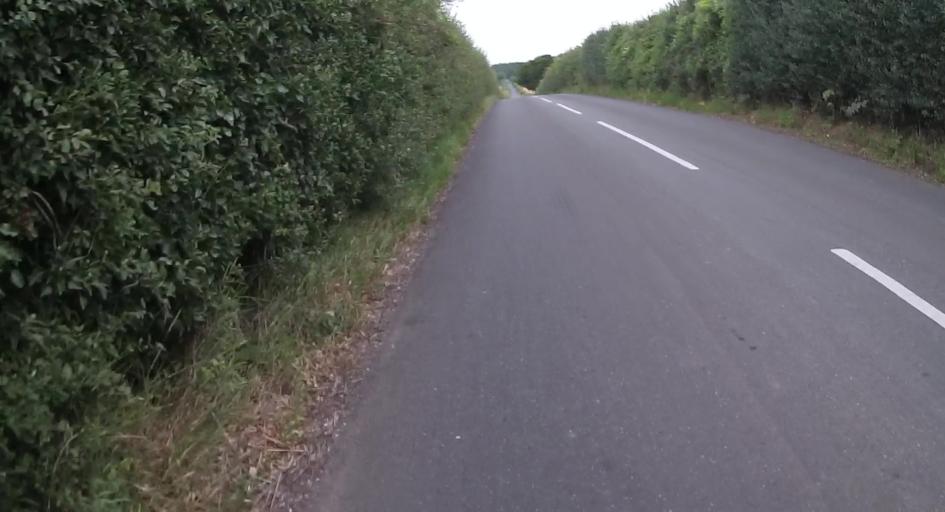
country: GB
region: England
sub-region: Hampshire
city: Kings Worthy
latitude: 51.1429
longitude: -1.3068
